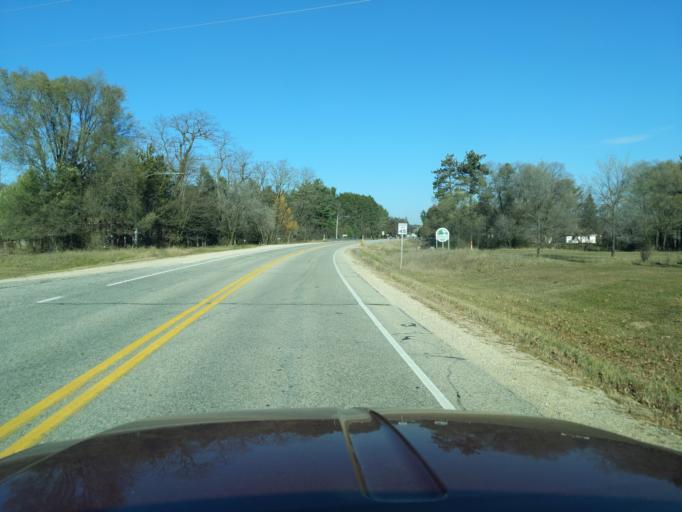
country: US
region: Wisconsin
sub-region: Waushara County
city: Wautoma
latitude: 44.0625
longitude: -89.2972
